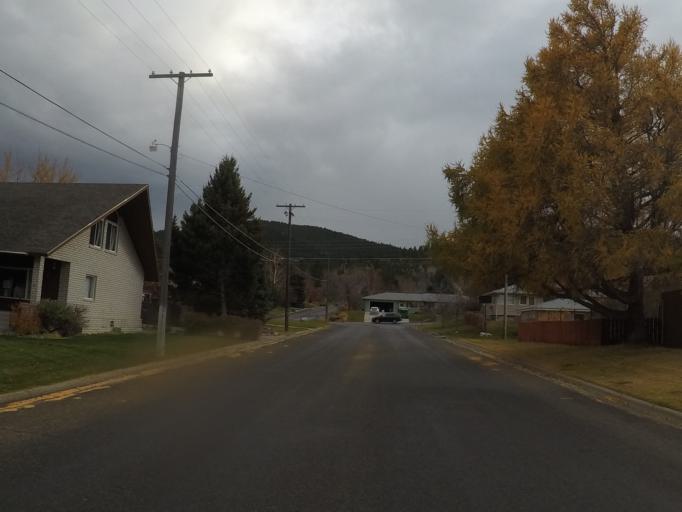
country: US
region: Montana
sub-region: Lewis and Clark County
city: Helena
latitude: 46.5822
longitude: -112.0146
